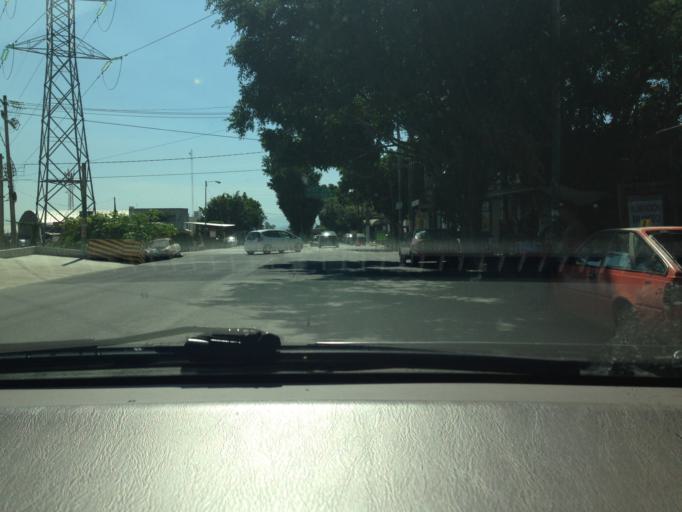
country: MX
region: Morelos
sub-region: Cuernavaca
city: Fraccionamiento Lomas de Ahuatlan
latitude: 18.9639
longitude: -99.2279
